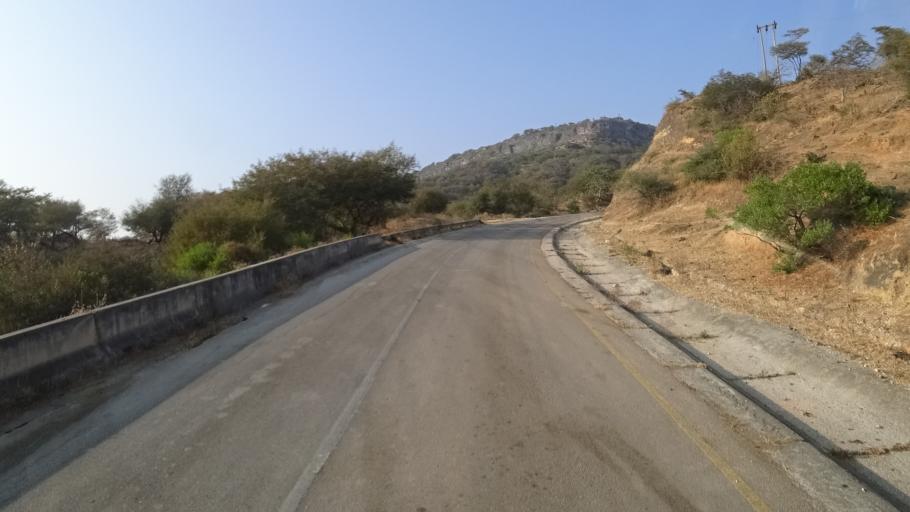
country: YE
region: Al Mahrah
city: Hawf
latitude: 16.7595
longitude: 53.3391
